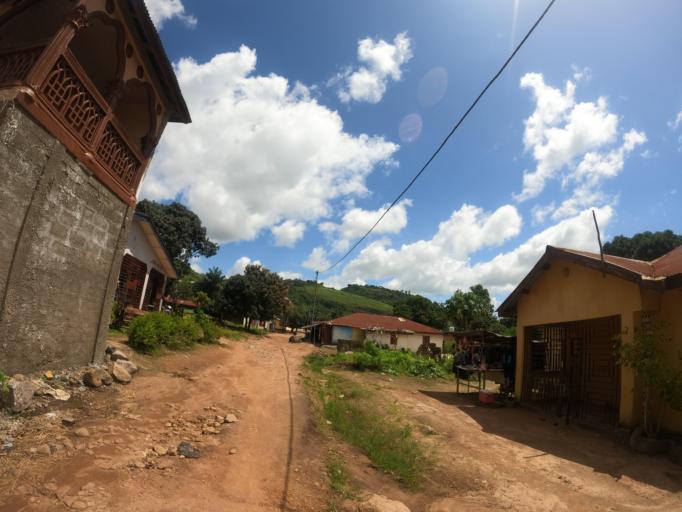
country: SL
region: Northern Province
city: Makeni
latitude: 8.8890
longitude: -12.0668
